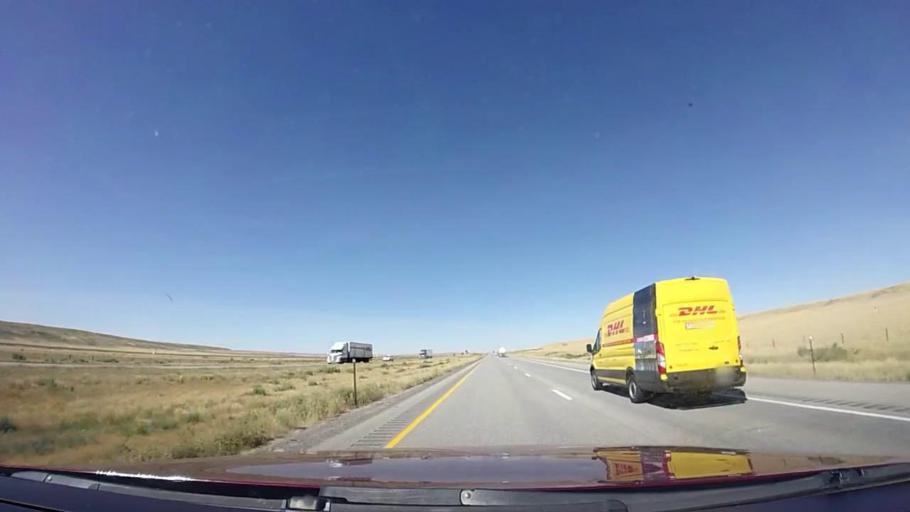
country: US
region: Wyoming
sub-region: Carbon County
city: Rawlins
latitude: 41.6571
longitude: -108.0948
